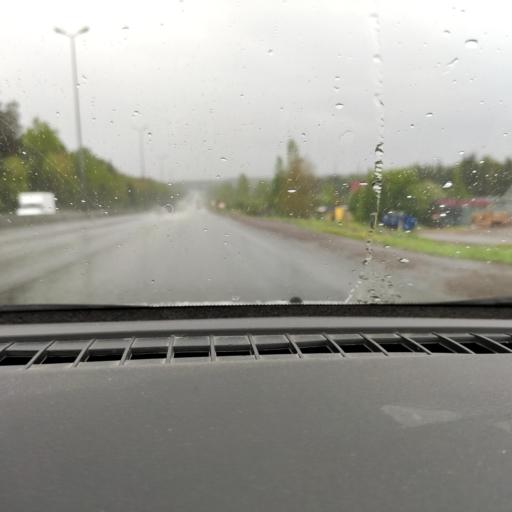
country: RU
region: Perm
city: Kondratovo
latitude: 58.0564
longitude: 56.1077
